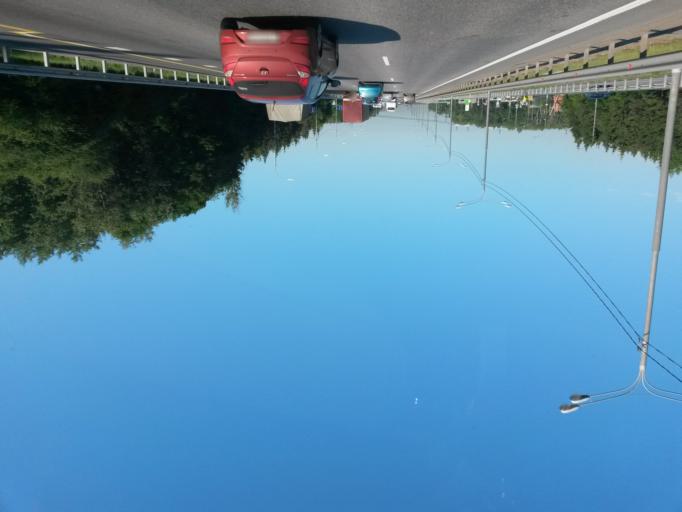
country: RU
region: Moskovskaya
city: Domodedovo
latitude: 55.4525
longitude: 37.7856
